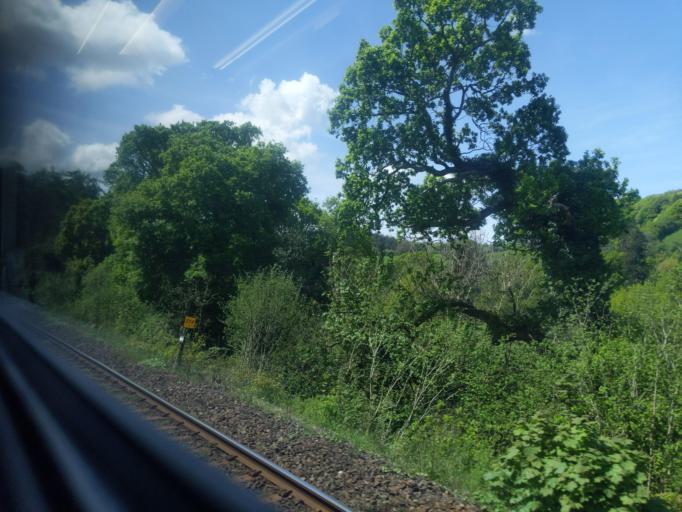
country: GB
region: England
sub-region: Cornwall
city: Lostwithiel
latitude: 50.4451
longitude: -4.6669
